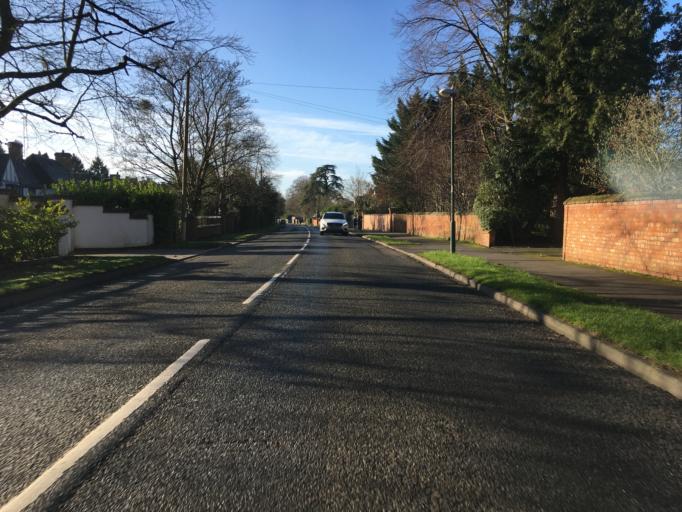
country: GB
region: England
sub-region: Warwickshire
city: Stratford-upon-Avon
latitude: 52.1945
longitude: -1.6928
